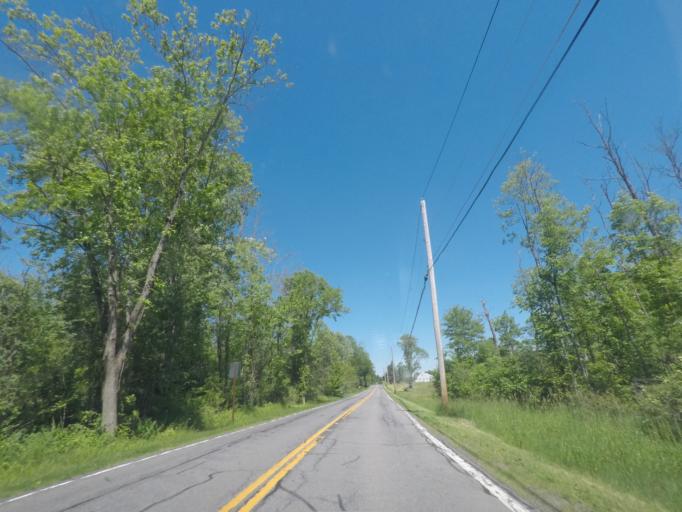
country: US
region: New York
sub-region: Saratoga County
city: Country Knolls
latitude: 42.8608
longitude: -73.8432
